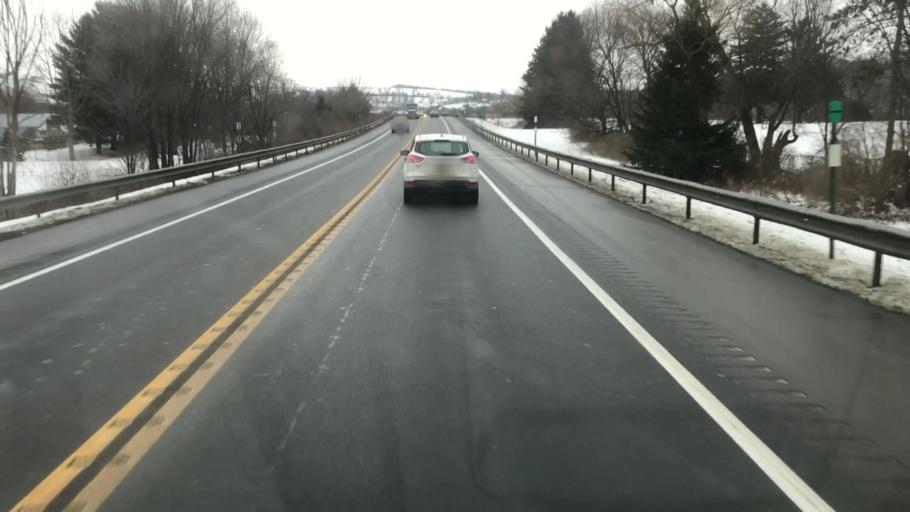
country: US
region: New York
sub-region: Cortland County
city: Homer
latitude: 42.6279
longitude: -76.1876
